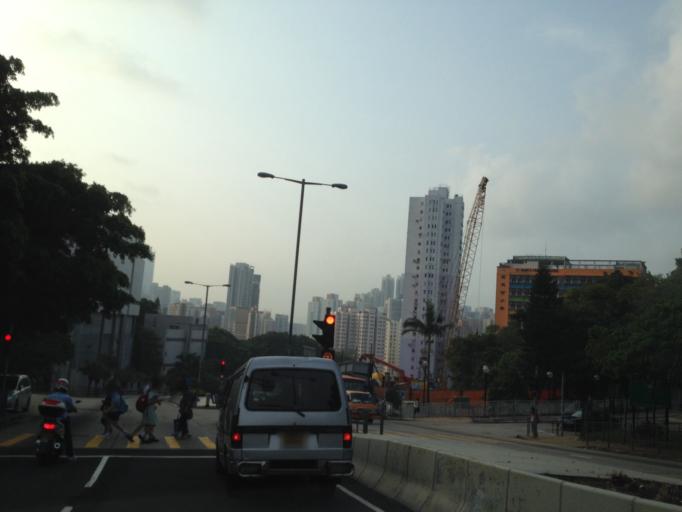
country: HK
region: Wanchai
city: Wan Chai
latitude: 22.2732
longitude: 114.2323
